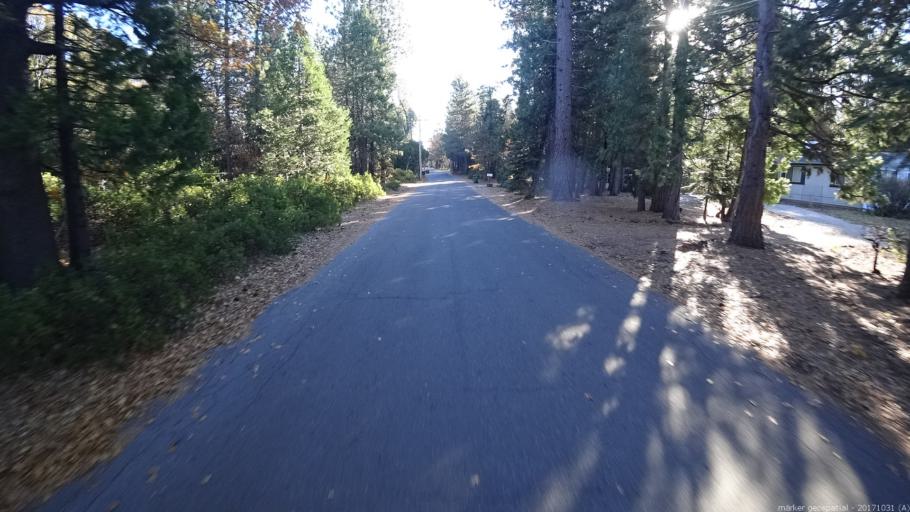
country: US
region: California
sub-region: Shasta County
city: Shingletown
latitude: 40.5180
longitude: -121.8275
